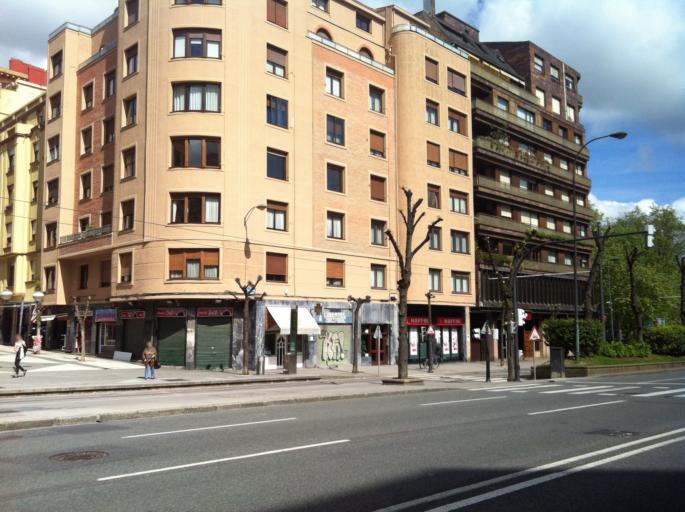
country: ES
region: Basque Country
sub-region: Bizkaia
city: Bilbao
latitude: 43.2631
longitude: -2.9461
